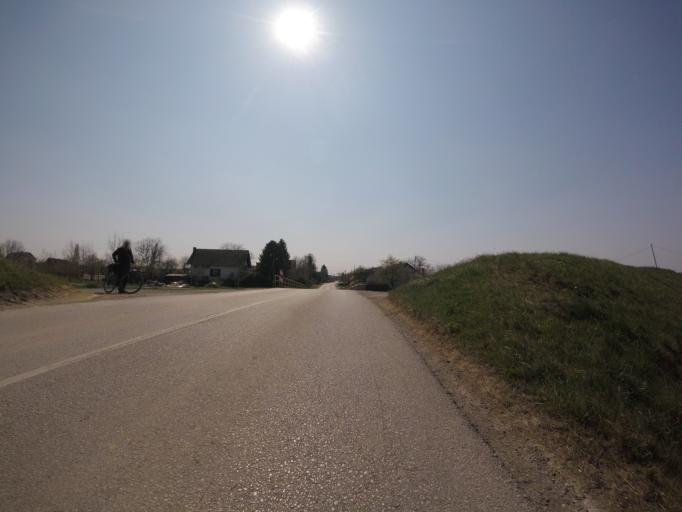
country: HR
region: Zagrebacka
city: Lukavec
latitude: 45.7087
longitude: 15.9947
